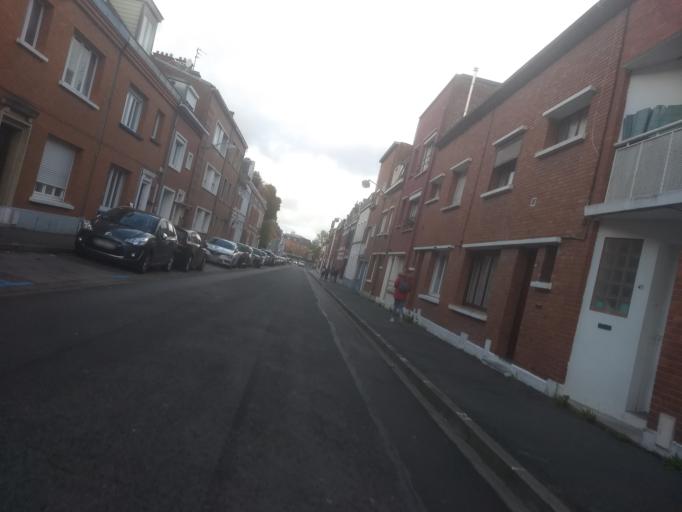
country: FR
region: Nord-Pas-de-Calais
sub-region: Departement du Pas-de-Calais
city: Arras
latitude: 50.2849
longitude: 2.7842
